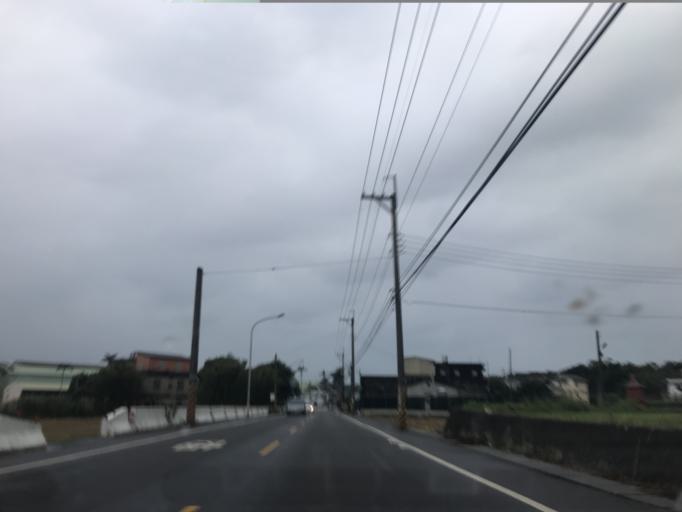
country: TW
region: Taiwan
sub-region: Hsinchu
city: Zhubei
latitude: 24.8321
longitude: 121.0902
